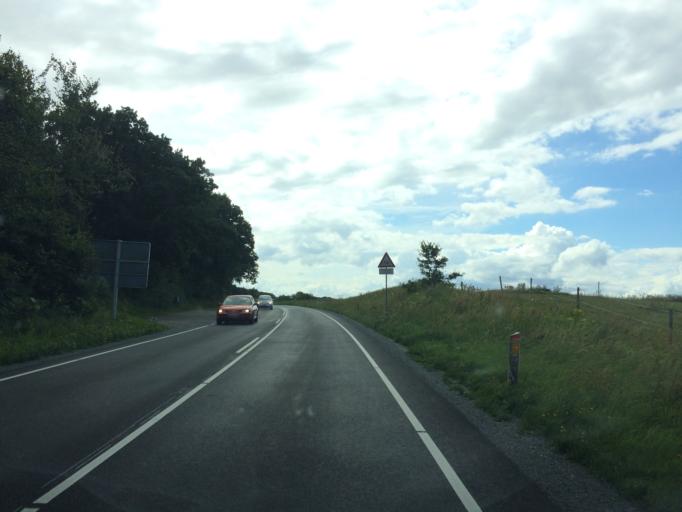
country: DK
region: South Denmark
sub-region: Faaborg-Midtfyn Kommune
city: Faaborg
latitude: 55.1476
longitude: 10.2645
